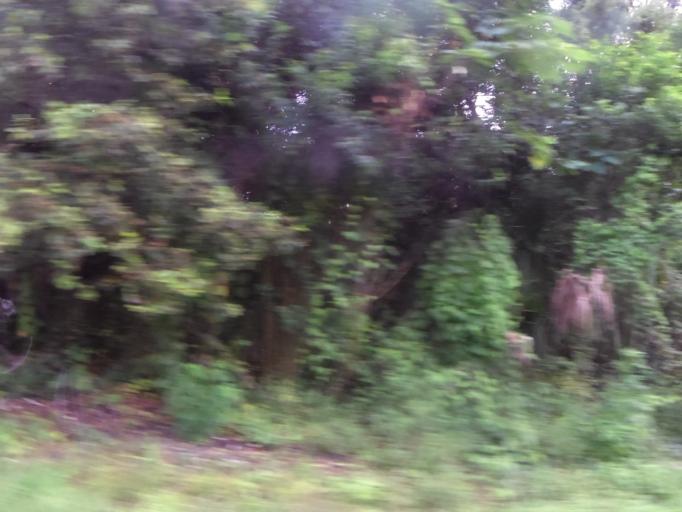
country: US
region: Florida
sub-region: Duval County
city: Jacksonville
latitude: 30.3561
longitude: -81.7170
